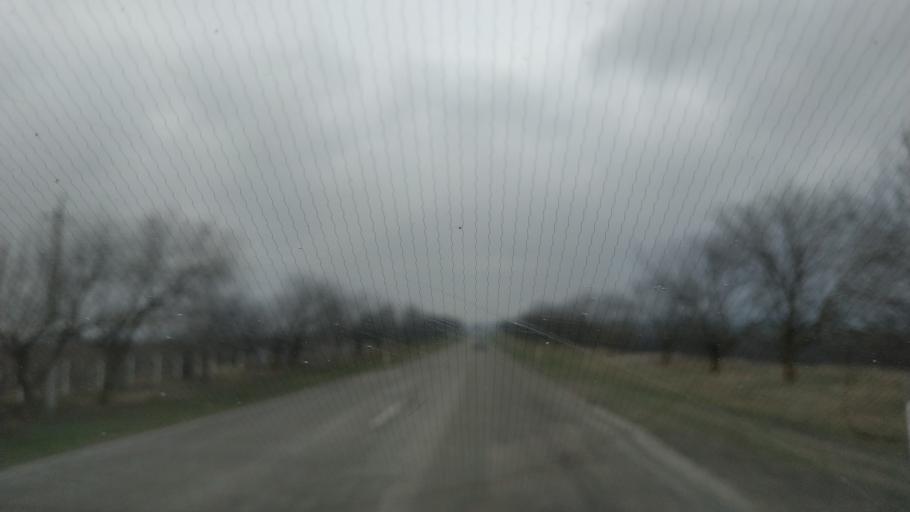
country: MD
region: Gagauzia
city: Comrat
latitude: 46.2642
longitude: 28.7420
